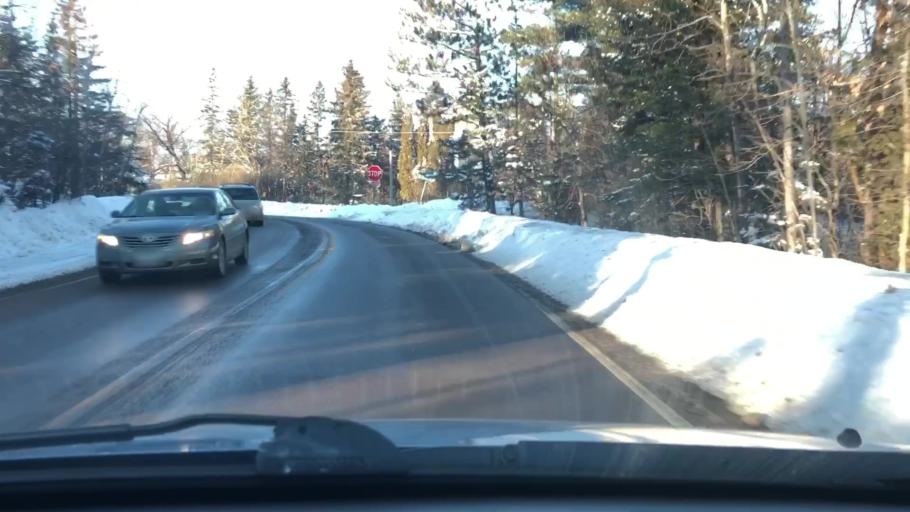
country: US
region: Minnesota
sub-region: Saint Louis County
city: Duluth
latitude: 46.8215
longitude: -92.0695
